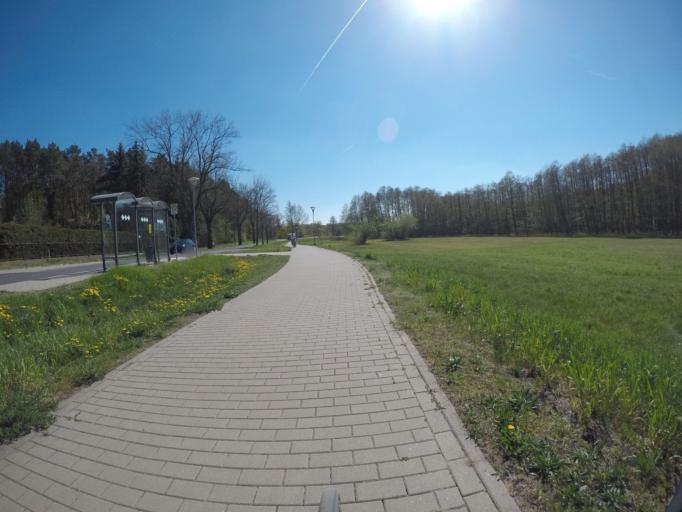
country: DE
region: Brandenburg
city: Strausberg
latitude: 52.5950
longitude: 13.8917
